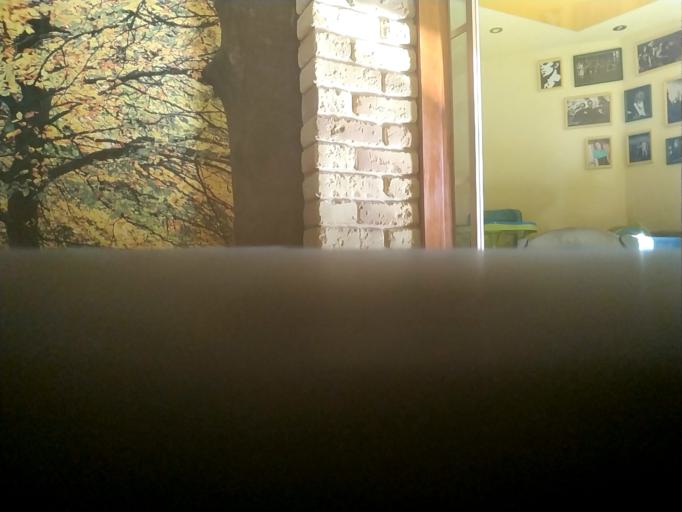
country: RU
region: Smolensk
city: Temkino
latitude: 54.9161
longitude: 34.9696
